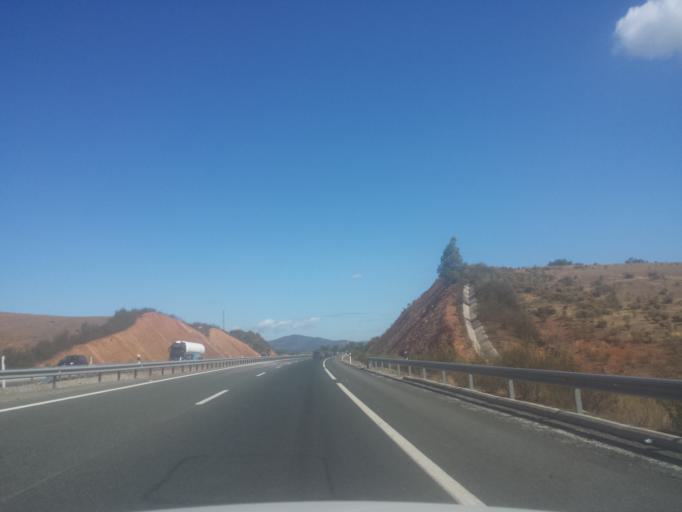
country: ES
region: Andalusia
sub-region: Provincia de Huelva
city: Santa Olalla del Cala
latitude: 37.8204
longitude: -6.2124
